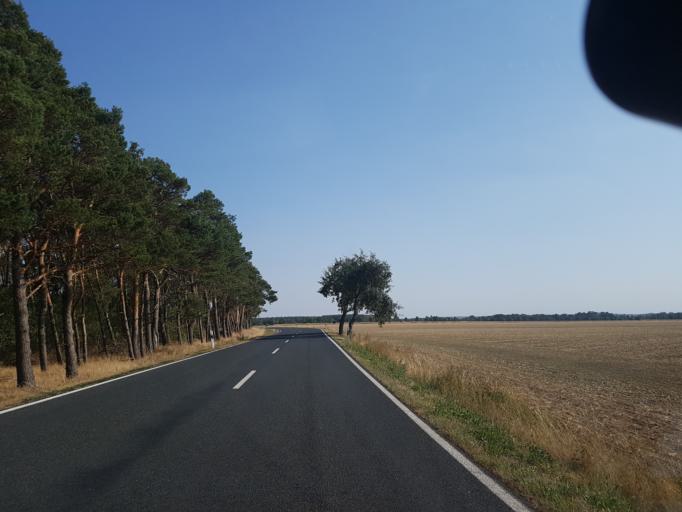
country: DE
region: Saxony
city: Beilrode
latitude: 51.5564
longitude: 13.0806
